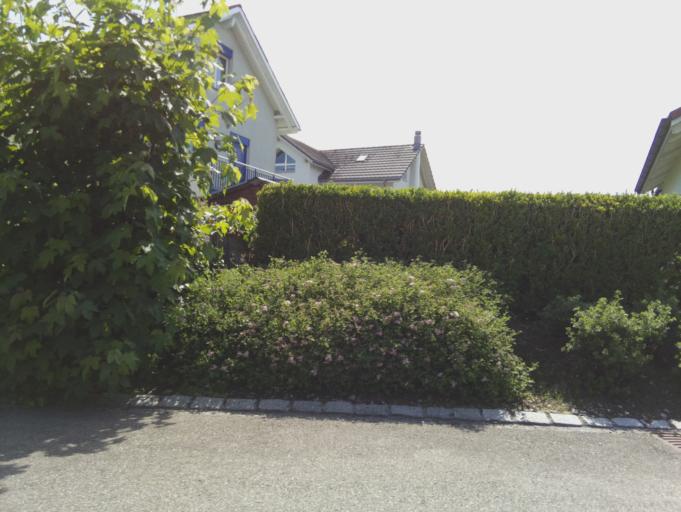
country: CH
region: Schwyz
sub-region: Bezirk March
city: Lachen
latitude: 47.1950
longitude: 8.8867
